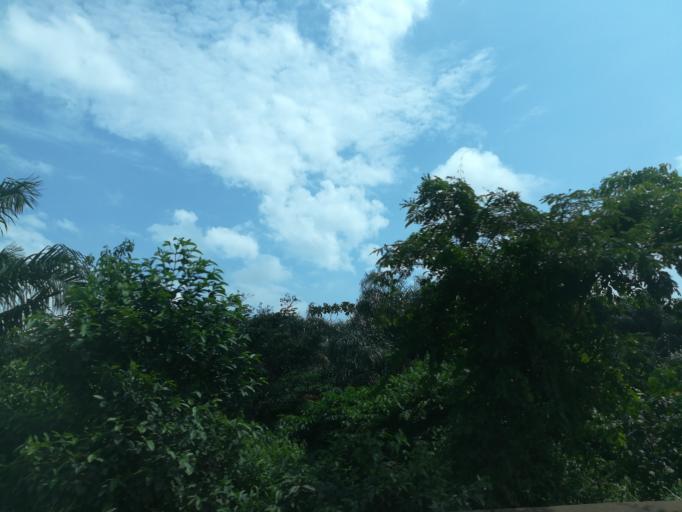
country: NG
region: Lagos
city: Ikorodu
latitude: 6.6575
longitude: 3.6870
